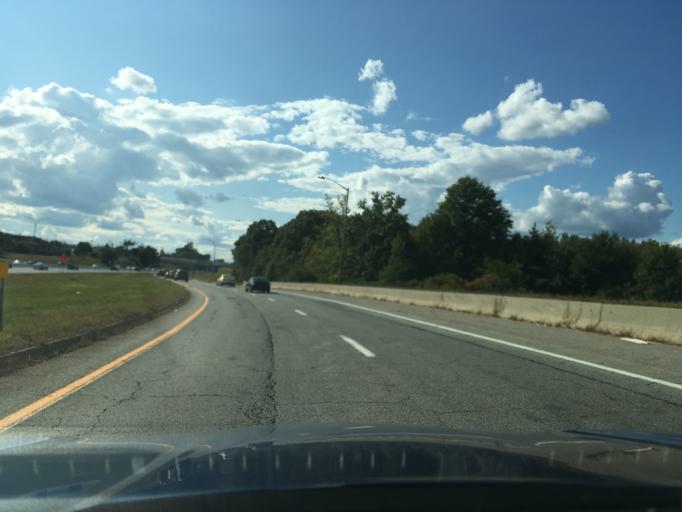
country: US
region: Massachusetts
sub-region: Bristol County
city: Seekonk
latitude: 41.8117
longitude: -71.3531
